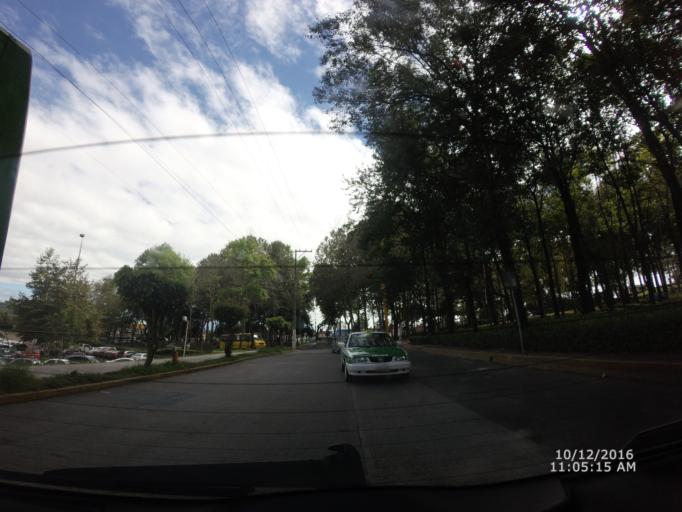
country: TR
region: Sivas
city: Karayun
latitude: 39.6723
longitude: 37.2342
